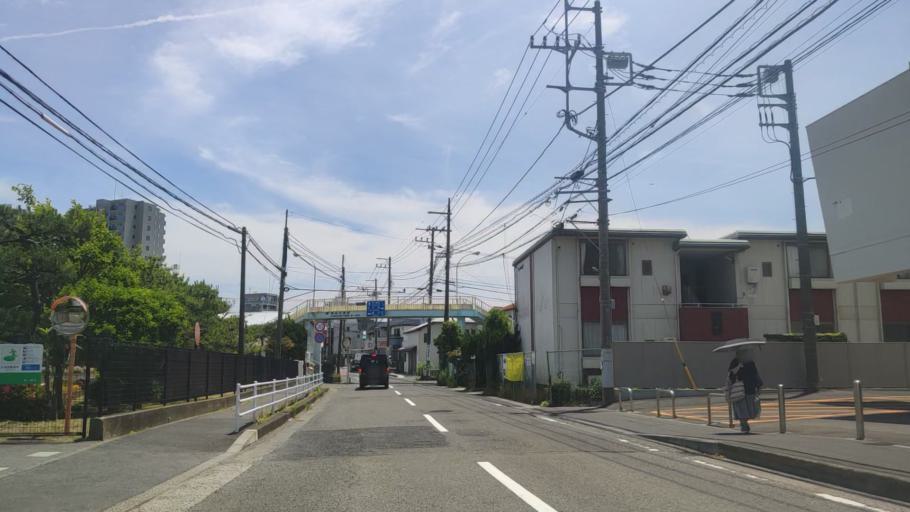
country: JP
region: Kanagawa
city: Chigasaki
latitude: 35.3329
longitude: 139.3999
